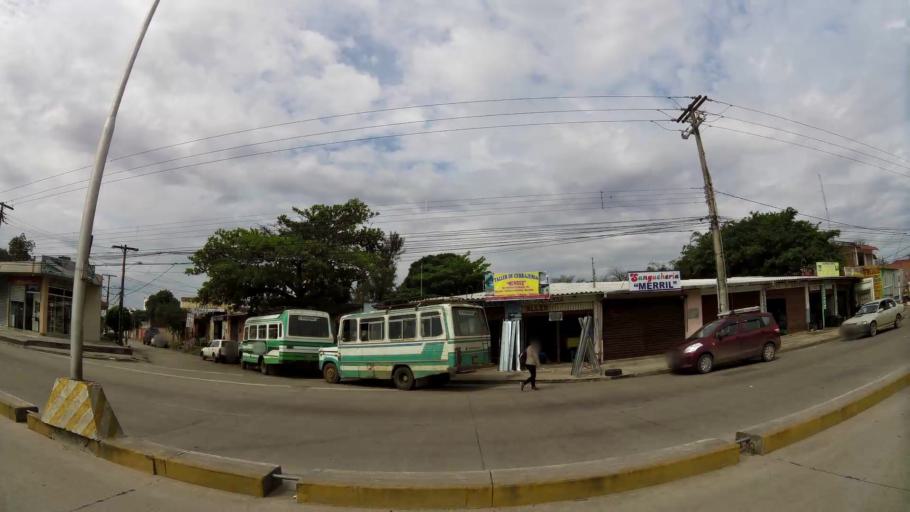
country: BO
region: Santa Cruz
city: Santa Cruz de la Sierra
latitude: -17.7768
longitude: -63.2034
